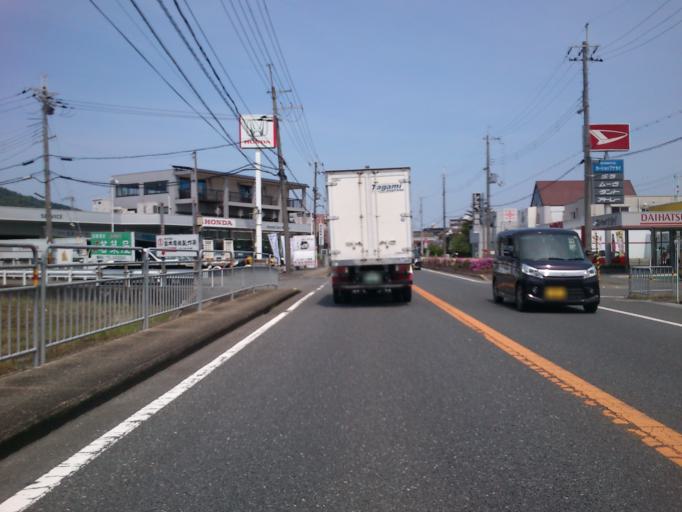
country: JP
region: Kyoto
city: Kameoka
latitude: 35.0288
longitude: 135.5547
